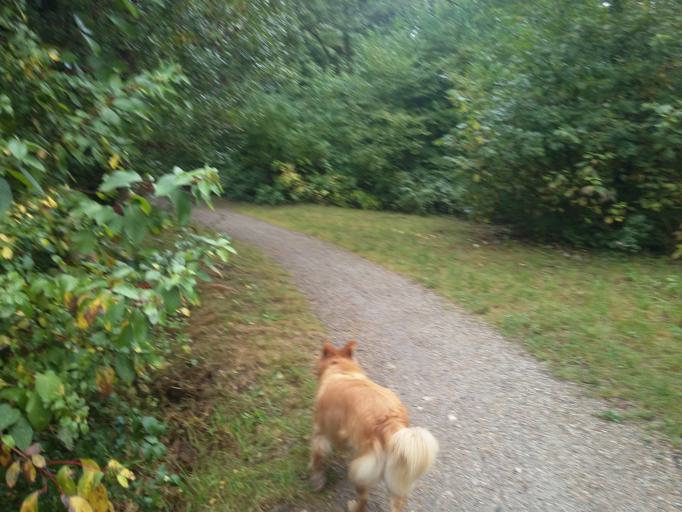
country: PL
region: Lodz Voivodeship
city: Lodz
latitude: 51.7543
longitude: 19.3976
